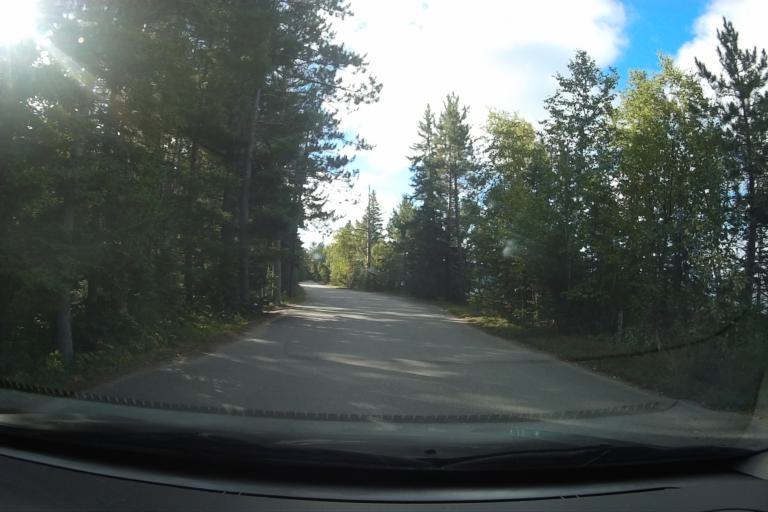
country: CA
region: Ontario
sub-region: Algoma
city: Sault Ste. Marie
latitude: 47.3318
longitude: -84.6149
